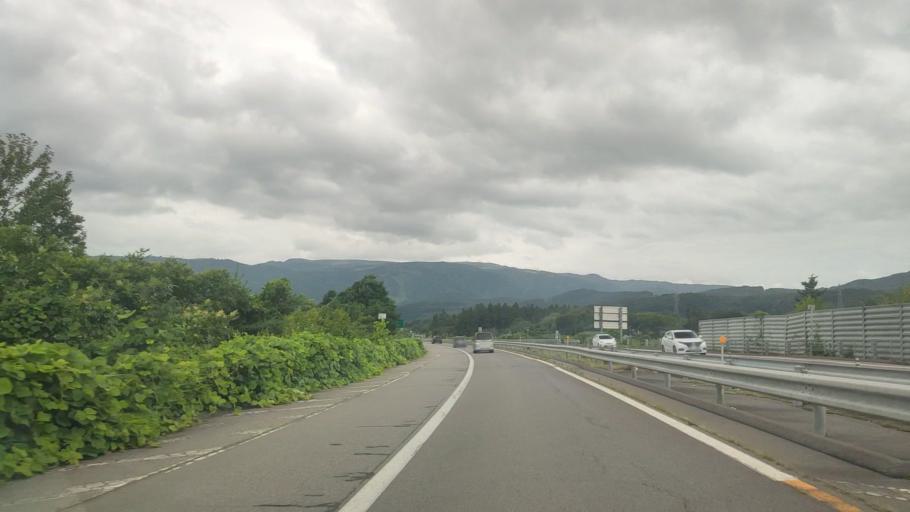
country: JP
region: Hokkaido
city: Nanae
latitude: 41.9203
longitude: 140.6794
